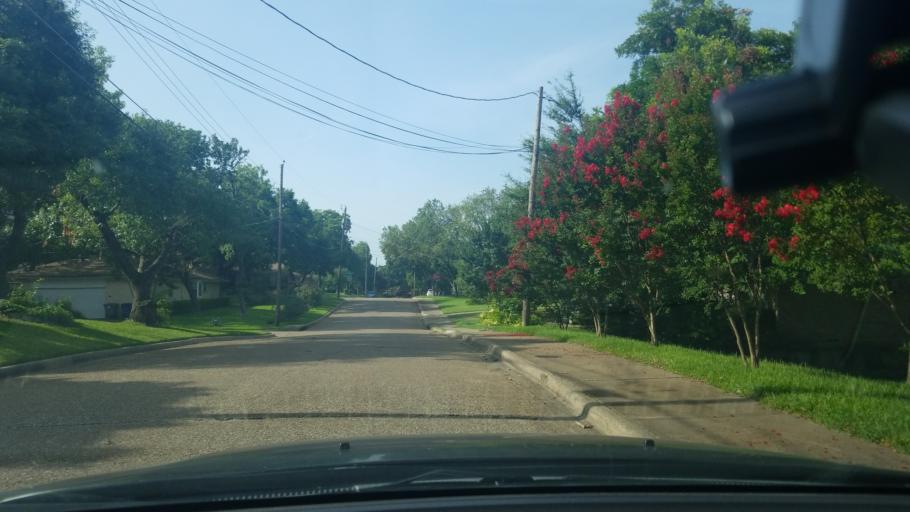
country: US
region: Texas
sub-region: Dallas County
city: Highland Park
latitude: 32.8001
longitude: -96.6980
